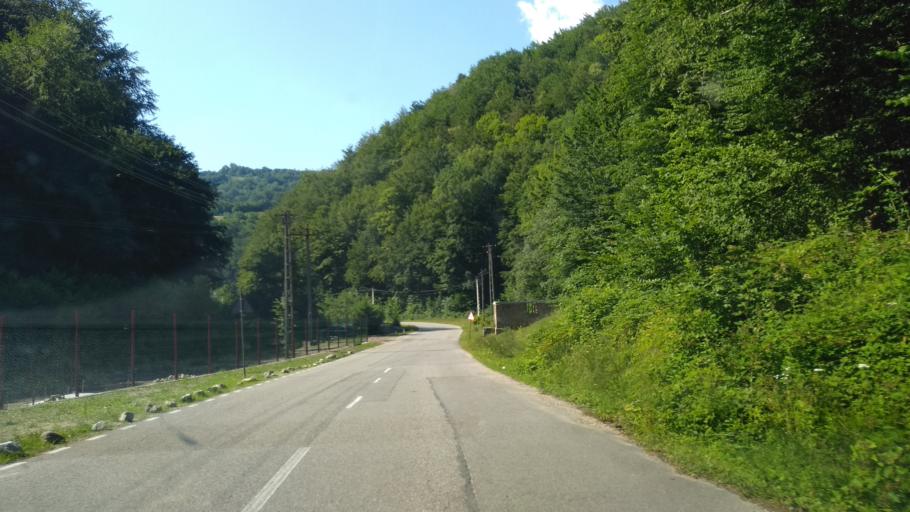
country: RO
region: Hunedoara
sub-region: Comuna Orastioara de Sus
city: Orastioara de Sus
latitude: 45.6284
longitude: 23.2187
